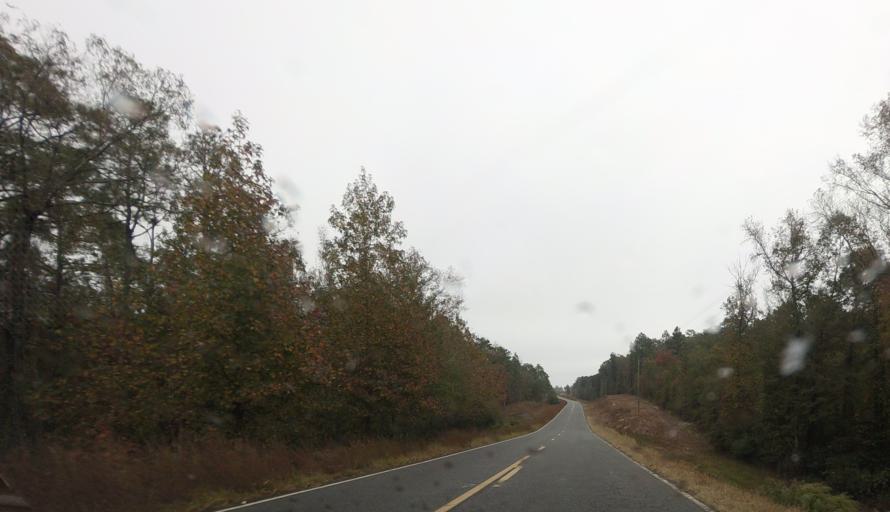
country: US
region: Georgia
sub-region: Taylor County
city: Butler
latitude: 32.4366
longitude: -84.3537
